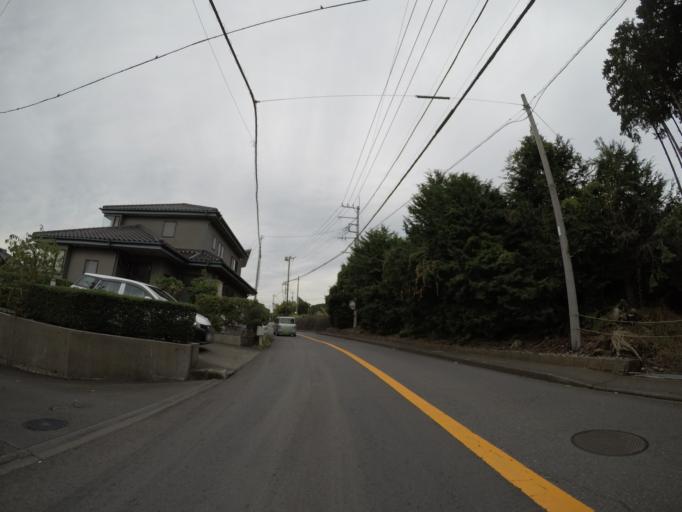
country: JP
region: Shizuoka
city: Fuji
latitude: 35.1884
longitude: 138.6952
